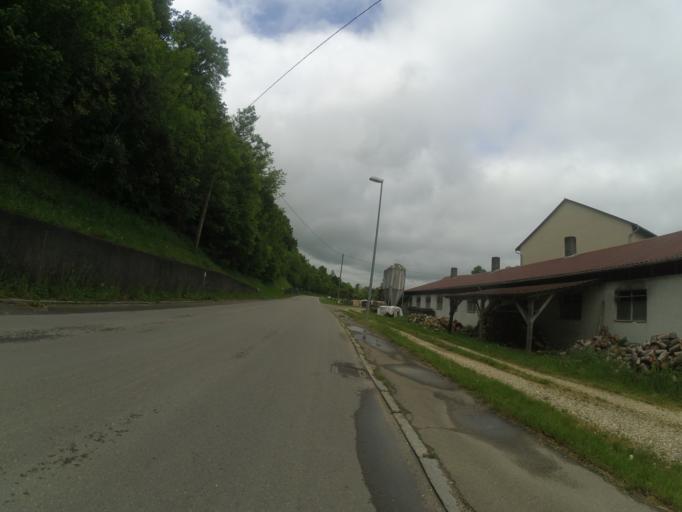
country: DE
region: Baden-Wuerttemberg
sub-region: Tuebingen Region
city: Bernstadt
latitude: 48.4835
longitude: 10.0541
